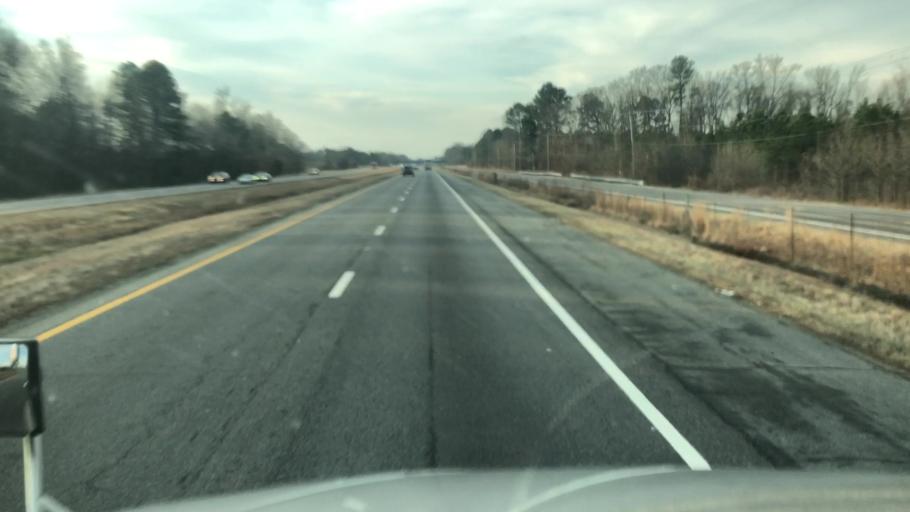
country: US
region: Virginia
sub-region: Sussex County
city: Sussex
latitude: 36.9162
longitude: -77.3973
